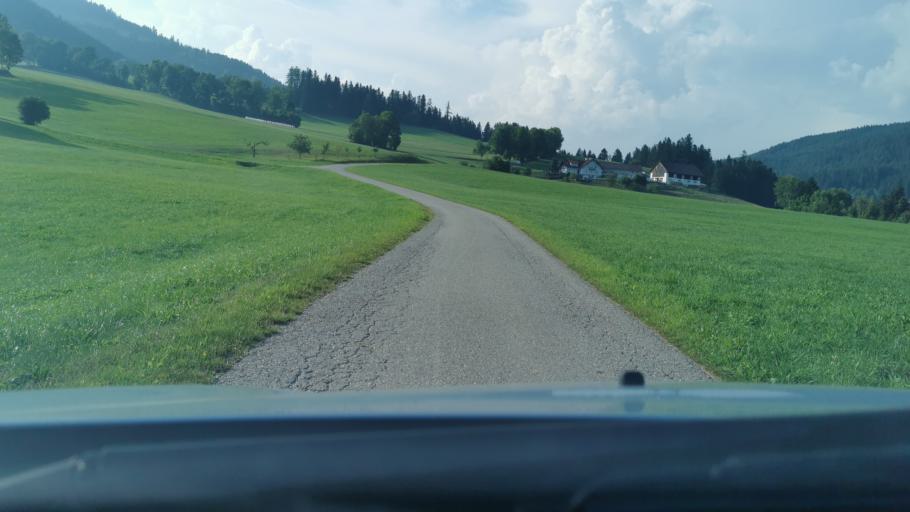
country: AT
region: Styria
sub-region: Politischer Bezirk Weiz
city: Fischbach
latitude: 47.3906
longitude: 15.6547
